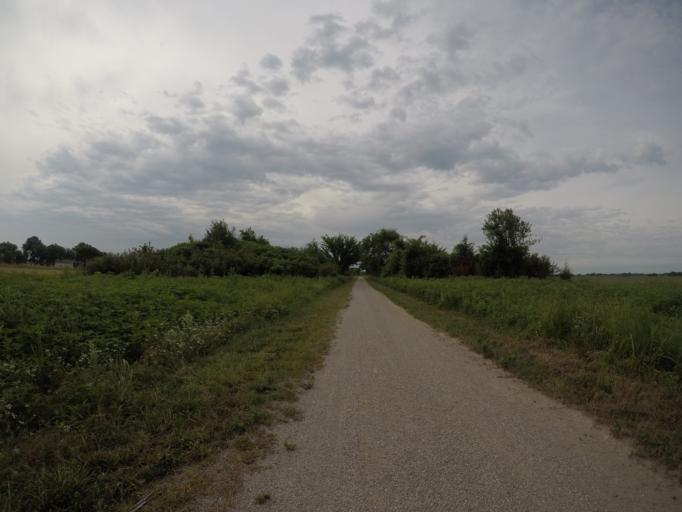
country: US
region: Kansas
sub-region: Franklin County
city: Ottawa
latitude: 38.4615
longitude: -95.2705
